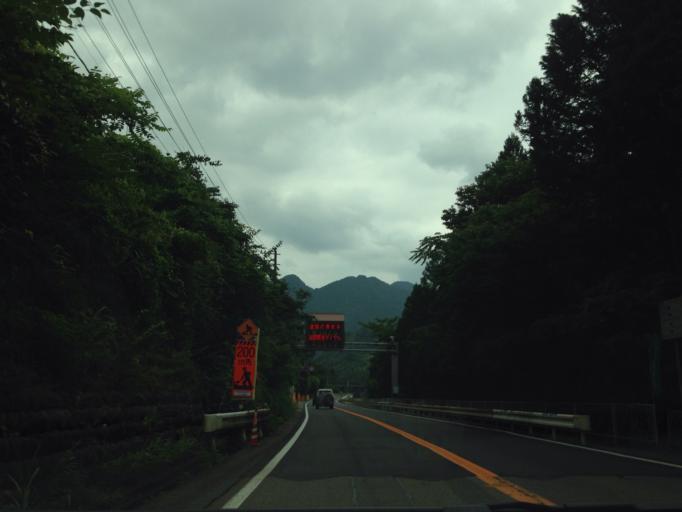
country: JP
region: Gifu
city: Mitake
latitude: 35.5909
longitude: 137.1702
